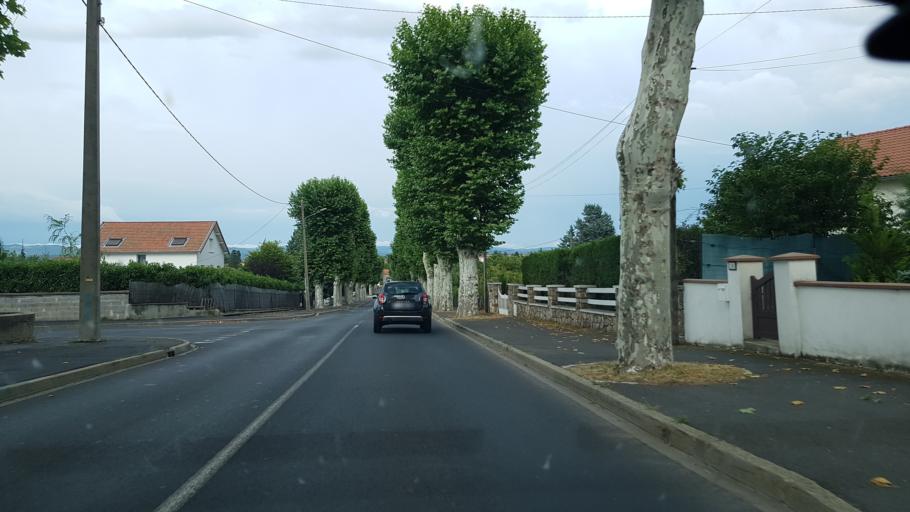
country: FR
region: Auvergne
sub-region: Departement de la Haute-Loire
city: Brioude
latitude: 45.2899
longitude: 3.3721
